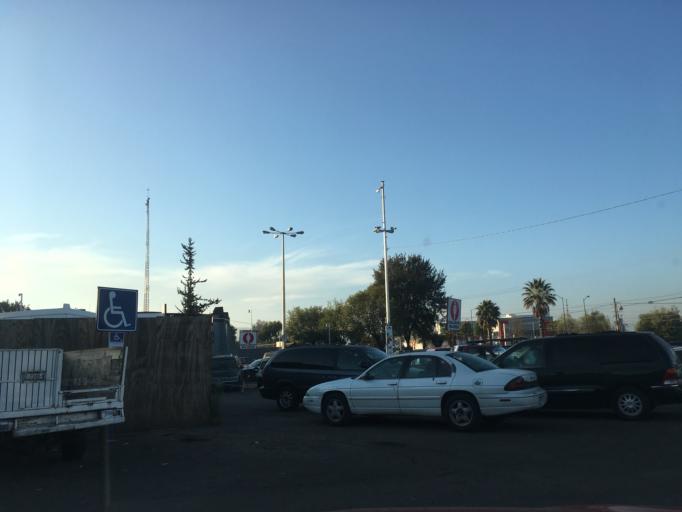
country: MX
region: Michoacan
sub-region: Morelia
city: Morelos
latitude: 19.6815
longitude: -101.2347
